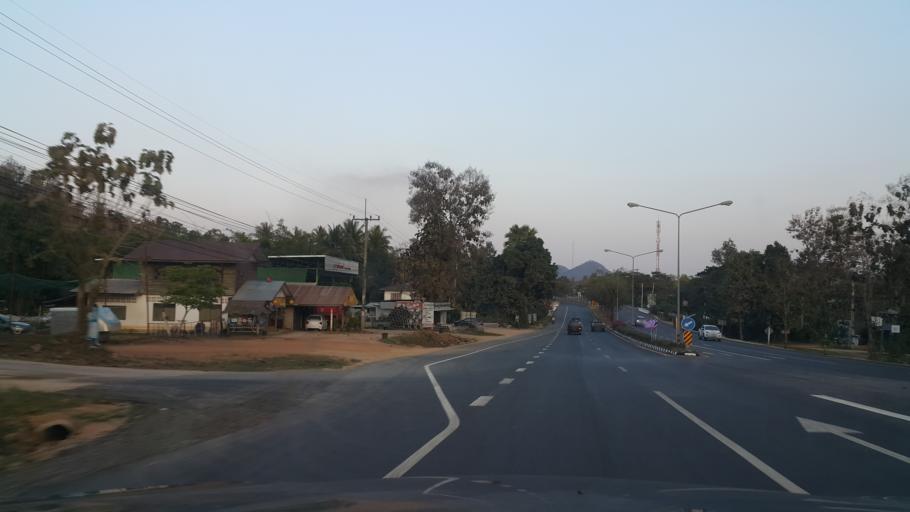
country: TH
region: Loei
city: Loei
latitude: 17.4910
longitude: 101.7003
